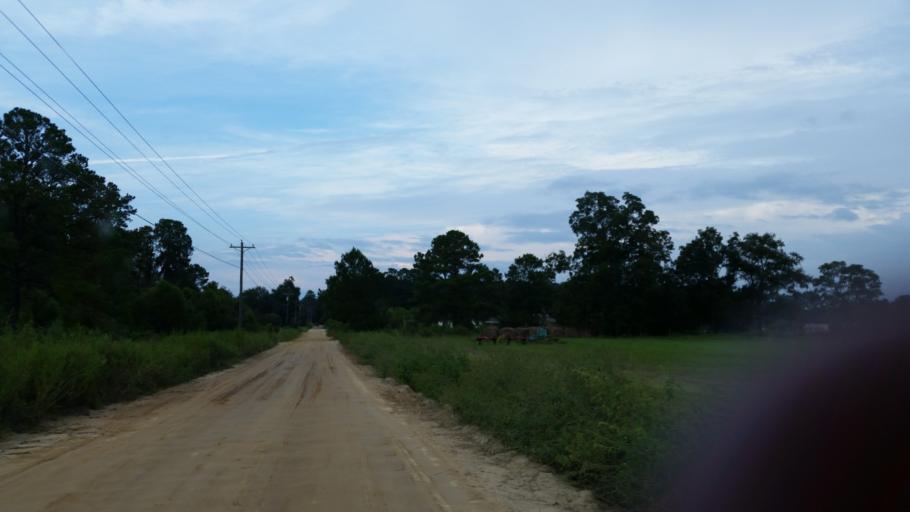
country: US
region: Georgia
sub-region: Lowndes County
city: Valdosta
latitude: 30.7217
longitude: -83.2977
